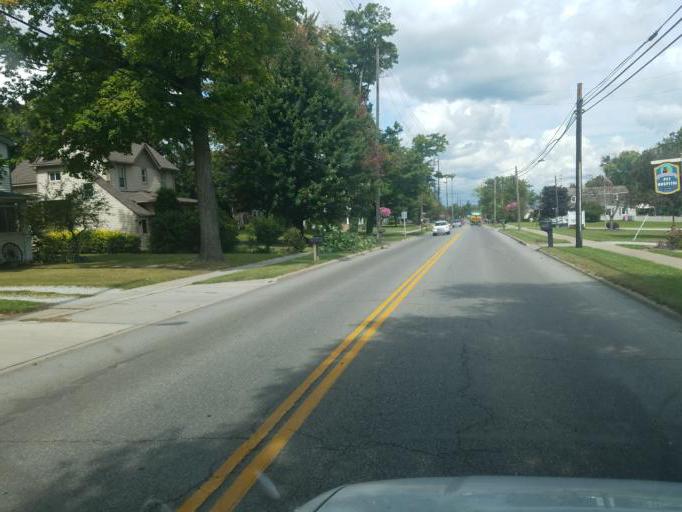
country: US
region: Ohio
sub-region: Geauga County
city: Middlefield
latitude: 41.4561
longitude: -81.0731
